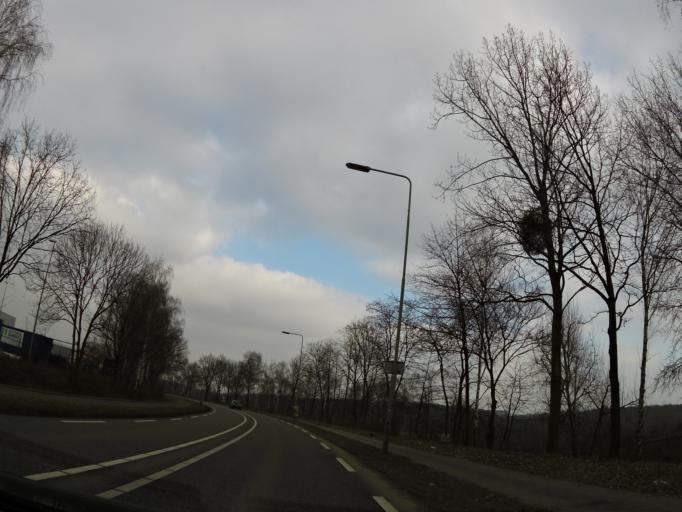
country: NL
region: Limburg
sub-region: Gemeente Kerkrade
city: Kerkrade
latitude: 50.8866
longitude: 6.0268
